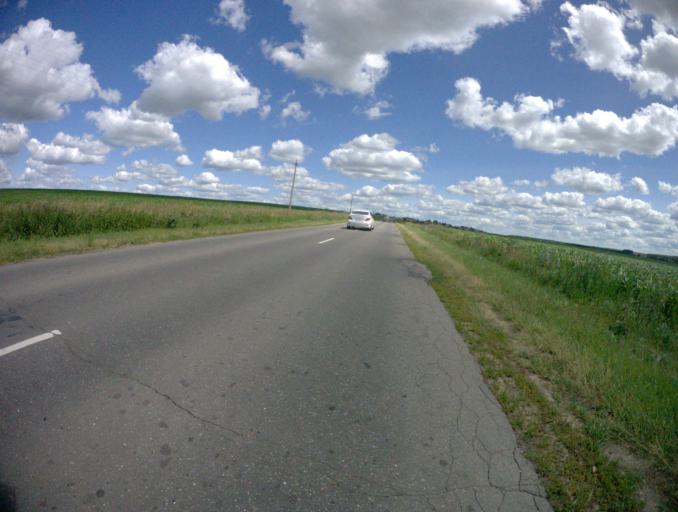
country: RU
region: Vladimir
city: Bogolyubovo
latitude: 56.2908
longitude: 40.5426
